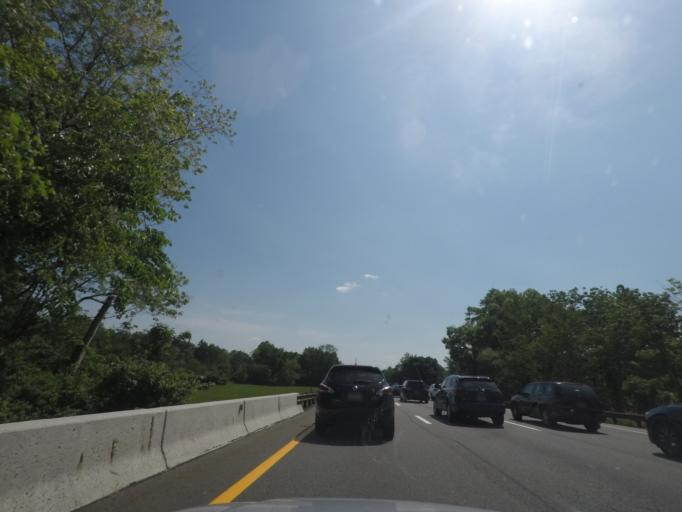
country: US
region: New Jersey
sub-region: Passaic County
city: Clifton
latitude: 40.8503
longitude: -74.1781
